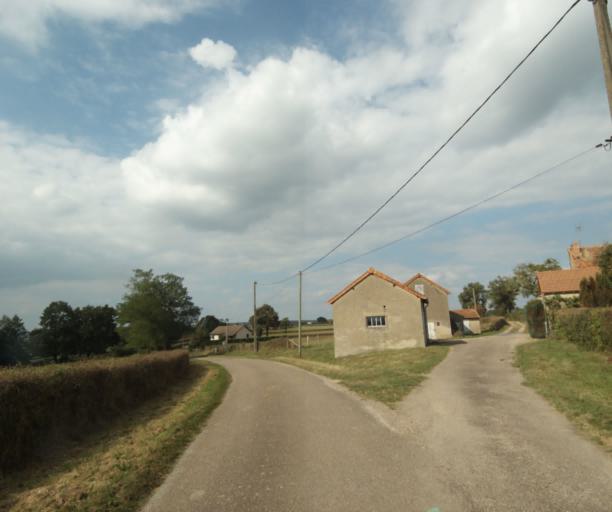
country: FR
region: Bourgogne
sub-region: Departement de Saone-et-Loire
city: Palinges
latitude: 46.4985
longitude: 4.1938
